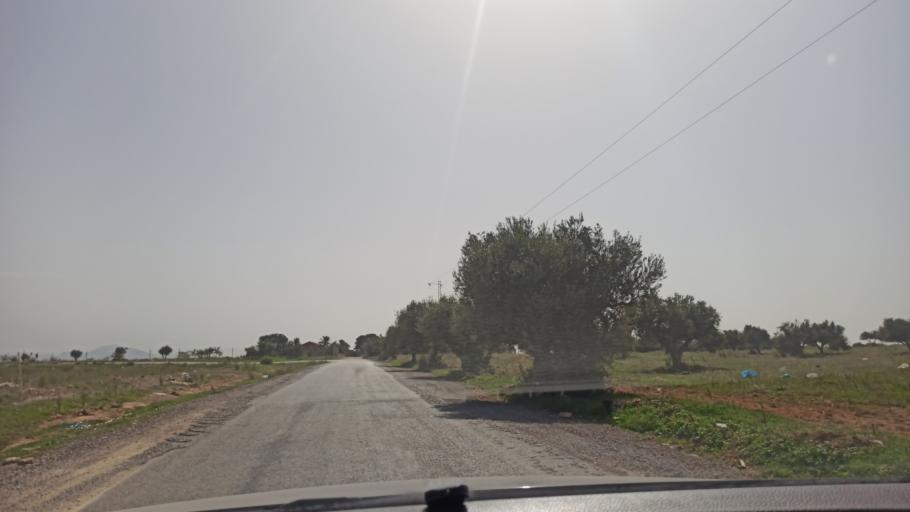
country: TN
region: Manouba
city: Manouba
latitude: 36.7340
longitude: 10.0867
